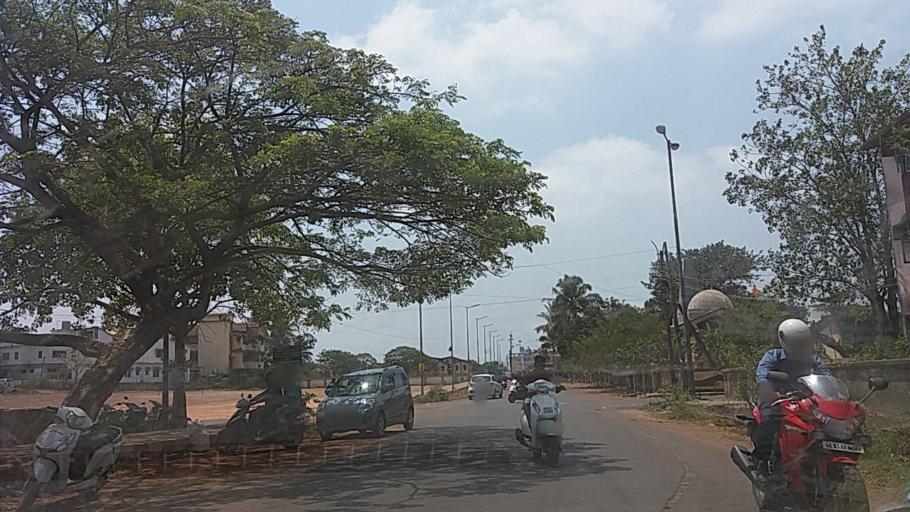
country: IN
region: Goa
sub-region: North Goa
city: Serula
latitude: 15.5272
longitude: 73.8332
